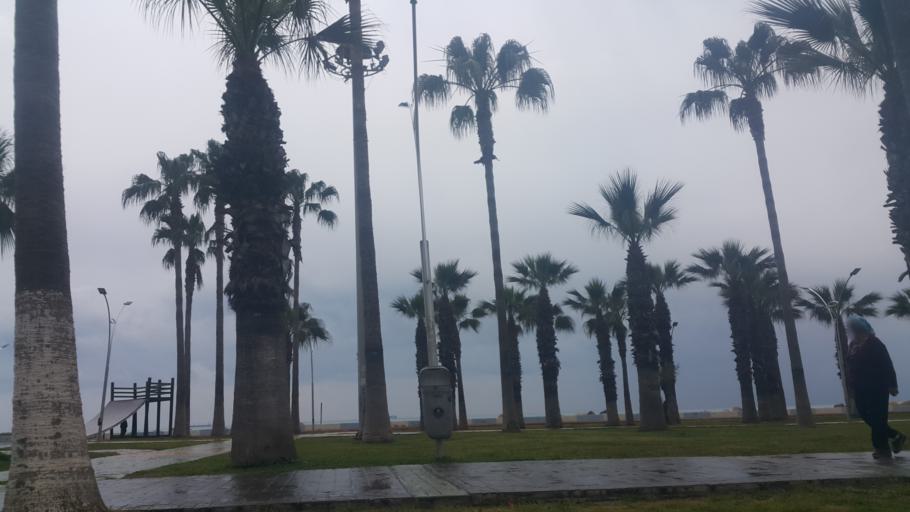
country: TR
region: Mersin
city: Mercin
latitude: 36.7805
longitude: 34.6044
